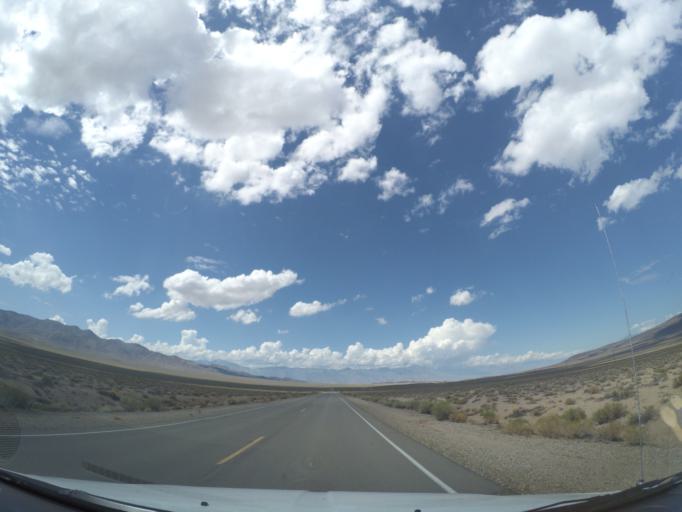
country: US
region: California
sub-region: Inyo County
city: Lone Pine
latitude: 36.3321
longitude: -117.7257
